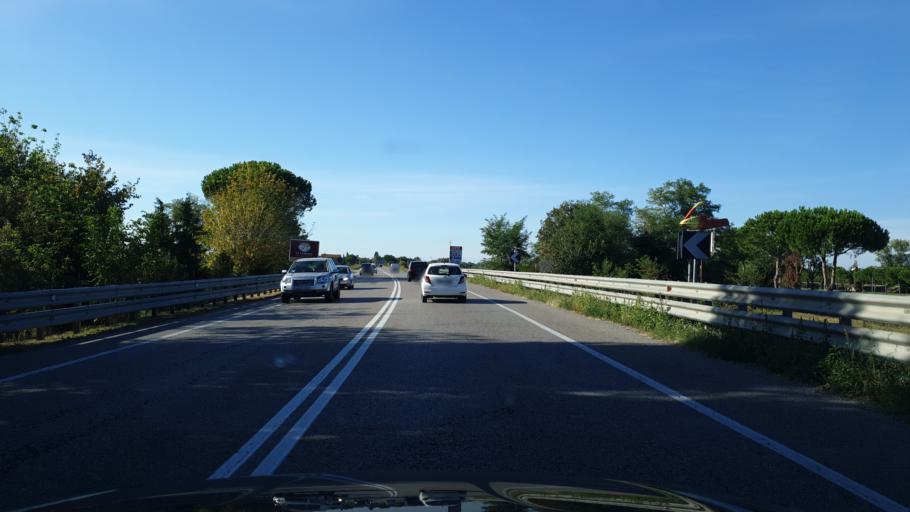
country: IT
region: Emilia-Romagna
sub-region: Provincia di Ravenna
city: Fosso Ghiaia
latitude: 44.3610
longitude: 12.2547
